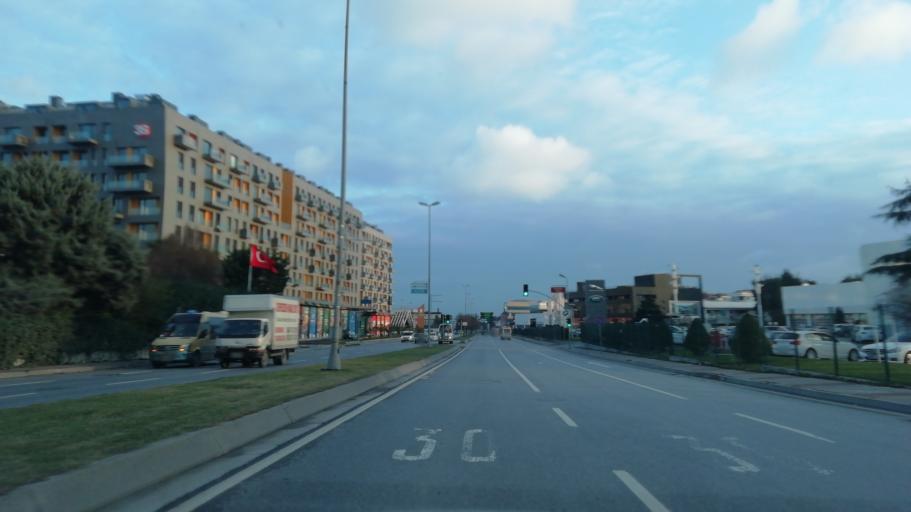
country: TR
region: Istanbul
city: Yakuplu
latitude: 40.9933
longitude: 28.7169
